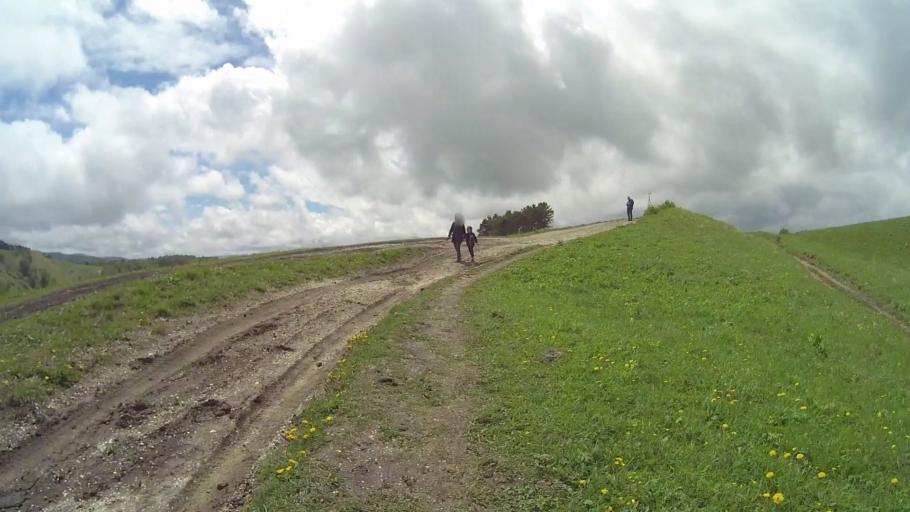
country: RU
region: Stavropol'skiy
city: Kislovodsk
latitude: 43.8862
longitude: 42.7682
